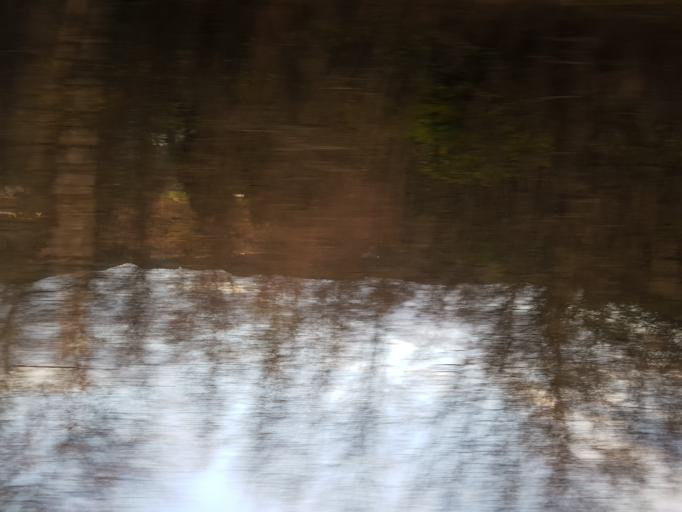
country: NO
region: Sor-Trondelag
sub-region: Melhus
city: Melhus
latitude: 63.2301
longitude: 10.2885
